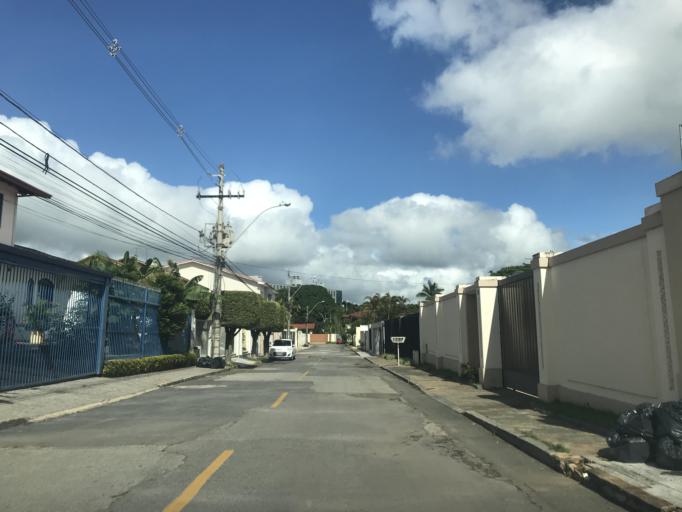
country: BR
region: Federal District
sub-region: Brasilia
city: Brasilia
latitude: -15.7226
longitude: -47.8785
